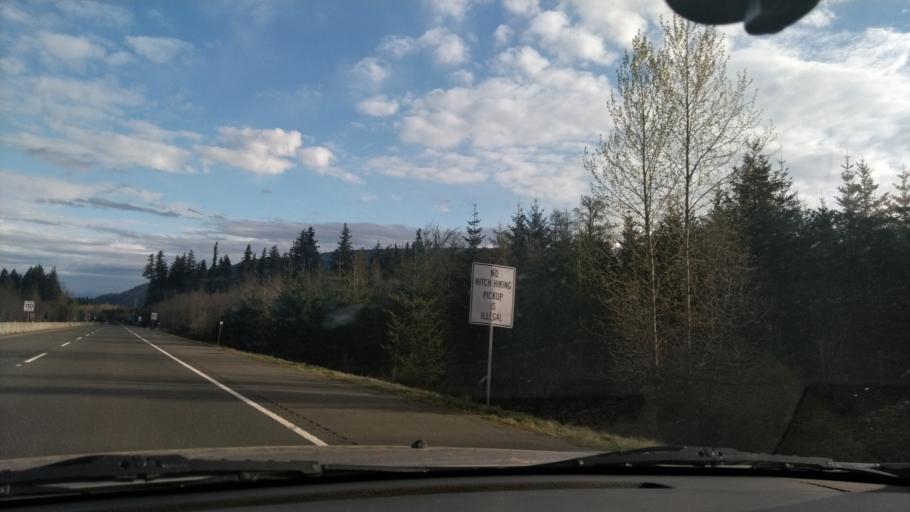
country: CA
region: British Columbia
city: Courtenay
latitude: 49.8014
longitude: -125.1614
